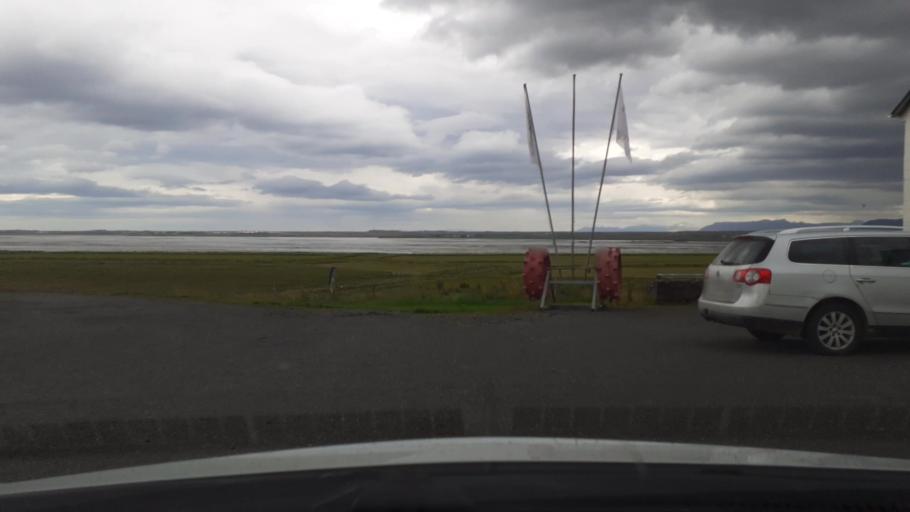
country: IS
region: West
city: Borgarnes
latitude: 64.5647
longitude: -21.7653
